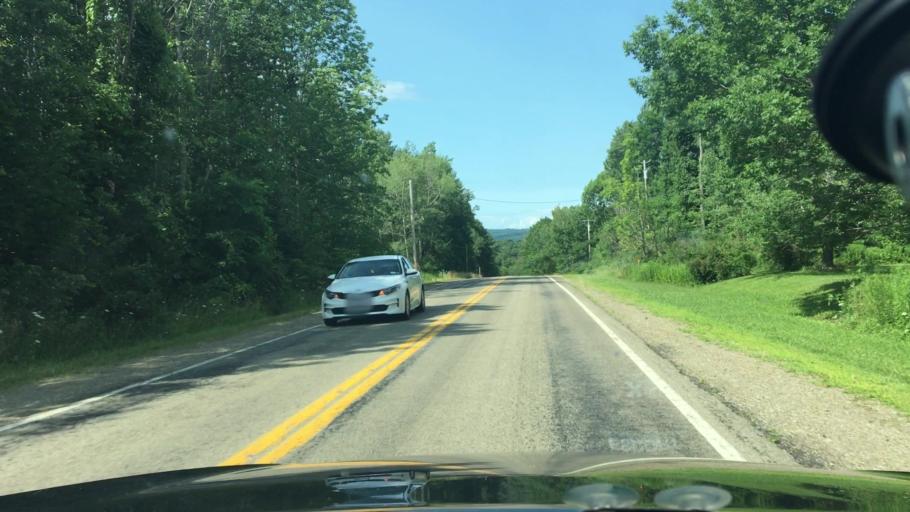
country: US
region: New York
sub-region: Chautauqua County
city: Lakewood
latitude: 42.2472
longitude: -79.3571
